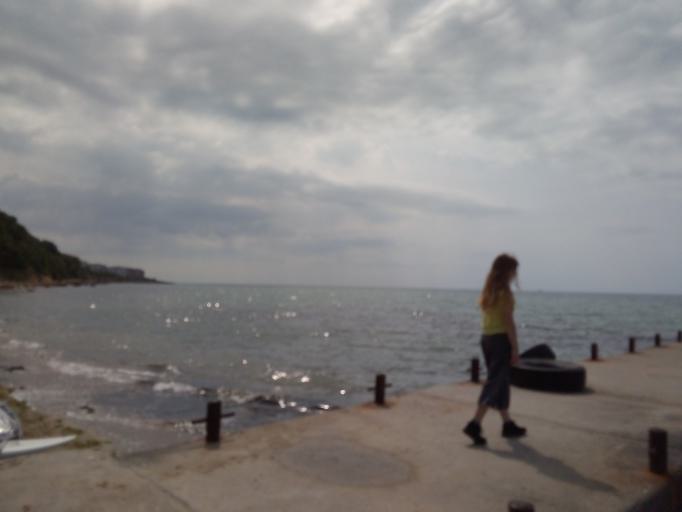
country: BG
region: Burgas
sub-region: Obshtina Nesebur
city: Sveti Vlas
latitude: 42.7056
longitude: 27.7789
